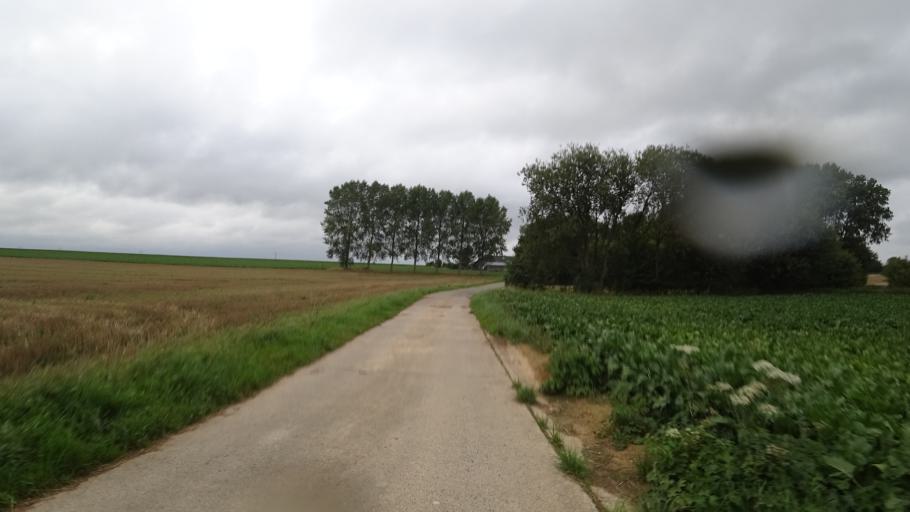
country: BE
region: Wallonia
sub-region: Province de Namur
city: Namur
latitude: 50.5391
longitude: 4.8331
